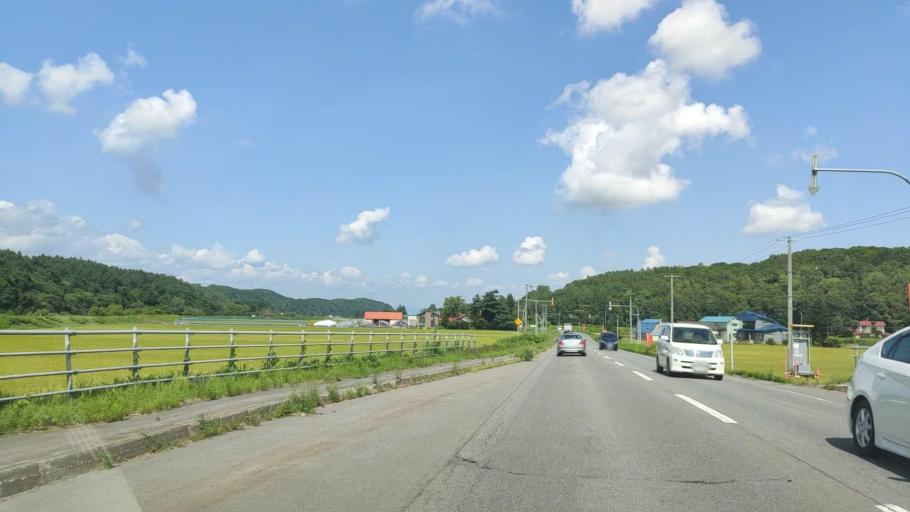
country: JP
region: Hokkaido
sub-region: Asahikawa-shi
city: Asahikawa
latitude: 43.6259
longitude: 142.4661
